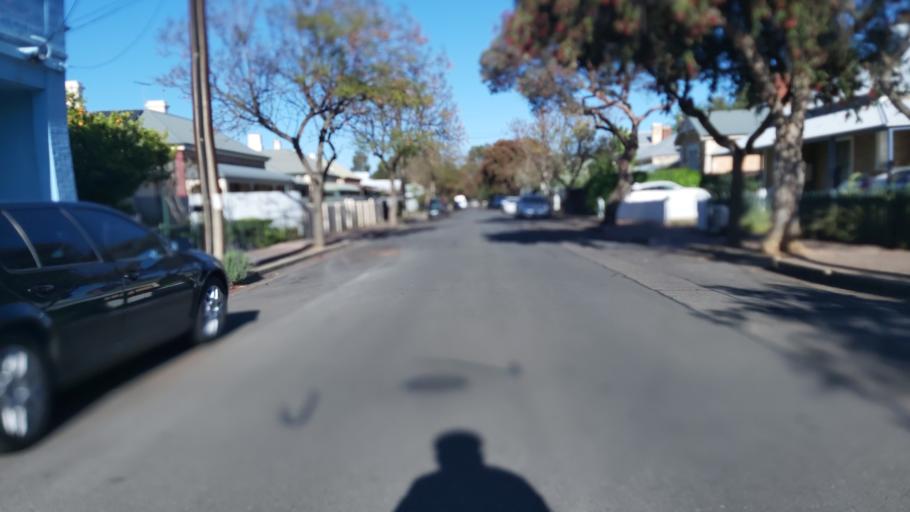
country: AU
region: South Australia
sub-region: Unley
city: Fullarton
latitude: -34.9478
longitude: 138.6181
